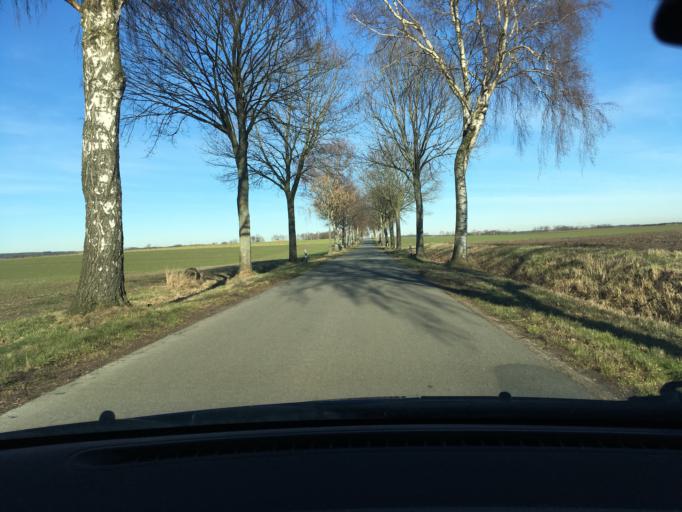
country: DE
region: Lower Saxony
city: Hanstedt Eins
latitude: 53.0302
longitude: 10.3644
